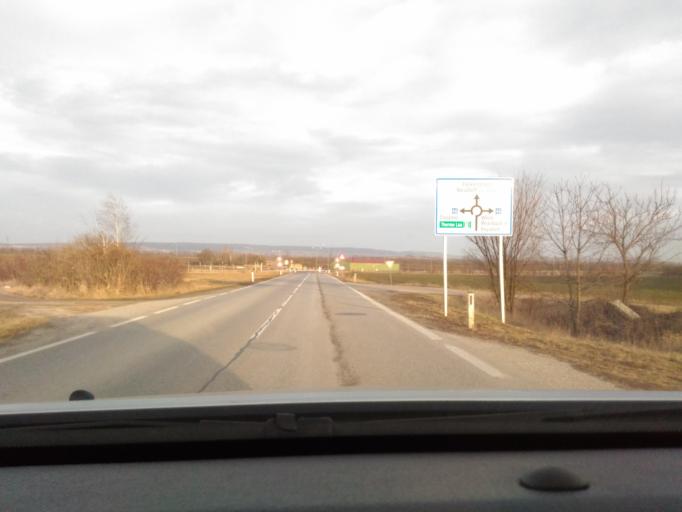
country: AT
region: Lower Austria
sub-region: Politischer Bezirk Mistelbach
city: Laa an der Thaya
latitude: 48.7224
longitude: 16.4181
